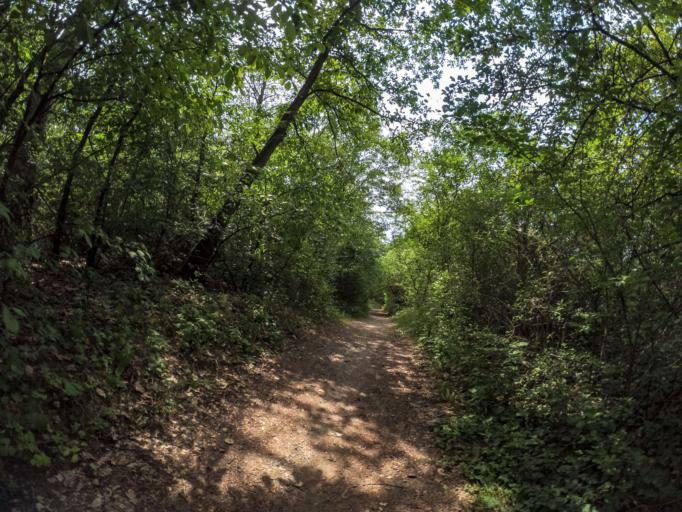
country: CZ
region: Central Bohemia
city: Neratovice
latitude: 50.2472
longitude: 14.5265
